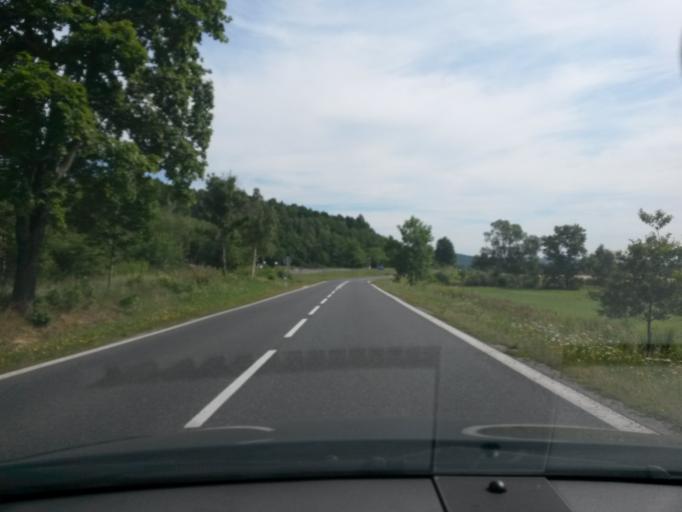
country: PL
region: Lower Silesian Voivodeship
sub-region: Powiat jeleniogorski
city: Piechowice
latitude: 50.8694
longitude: 15.6130
